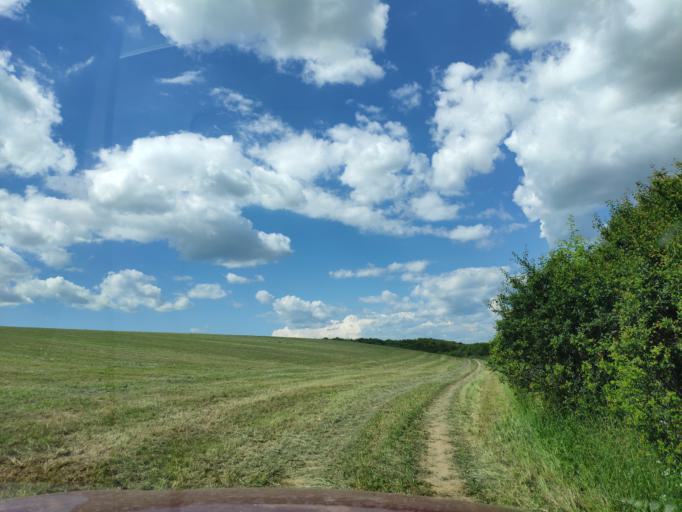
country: HU
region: Borsod-Abauj-Zemplen
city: Arlo
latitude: 48.2715
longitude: 20.1982
